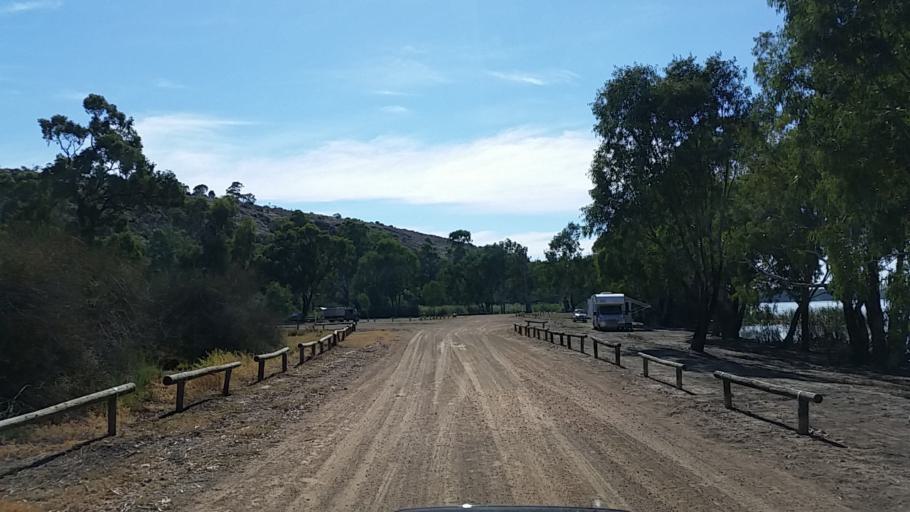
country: AU
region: South Australia
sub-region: Mid Murray
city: Mannum
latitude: -34.7010
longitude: 139.5756
